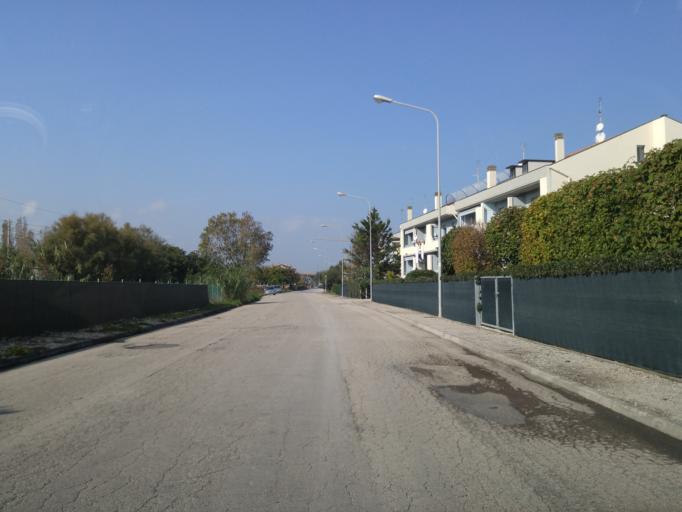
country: IT
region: The Marches
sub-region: Provincia di Pesaro e Urbino
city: Fano
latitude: 43.8359
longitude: 13.0406
